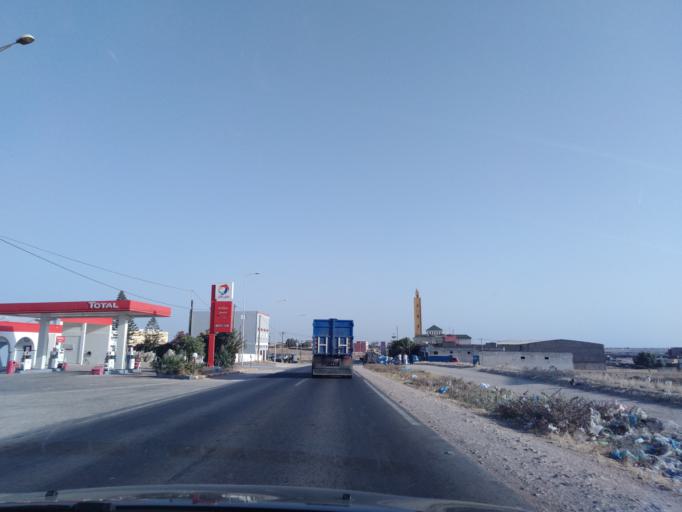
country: MA
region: Doukkala-Abda
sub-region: El-Jadida
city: Sidi Bennour
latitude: 32.5568
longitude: -8.7250
